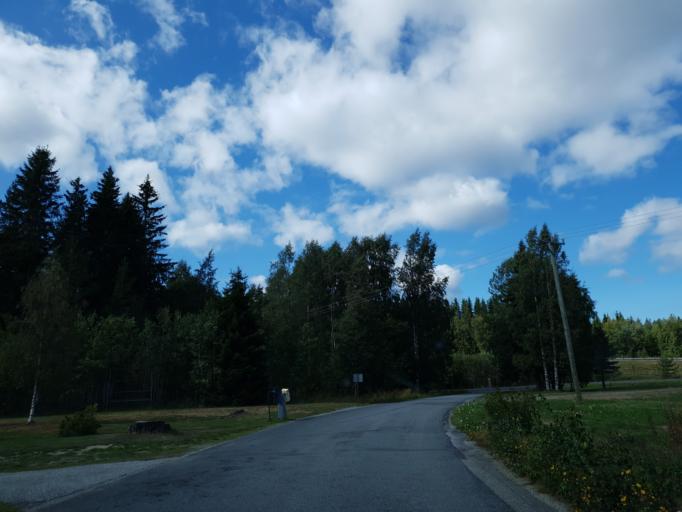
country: SE
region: Vaesternorrland
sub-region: OErnskoeldsviks Kommun
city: Husum
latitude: 63.3404
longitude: 19.1137
